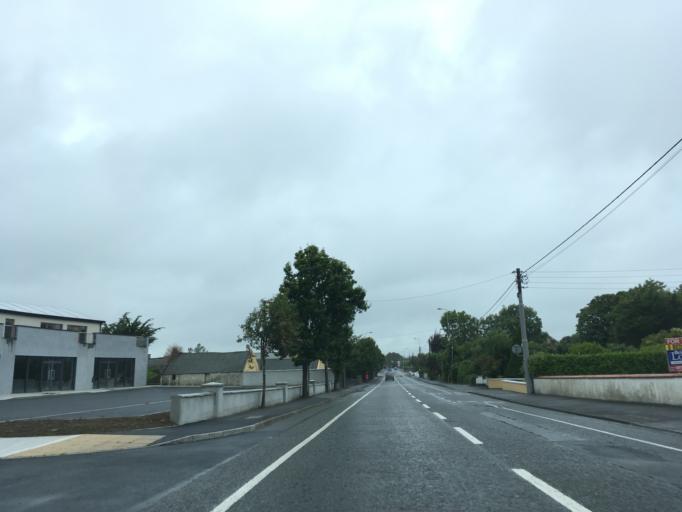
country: IE
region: Munster
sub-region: An Clar
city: Ennis
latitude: 52.8265
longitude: -8.9784
